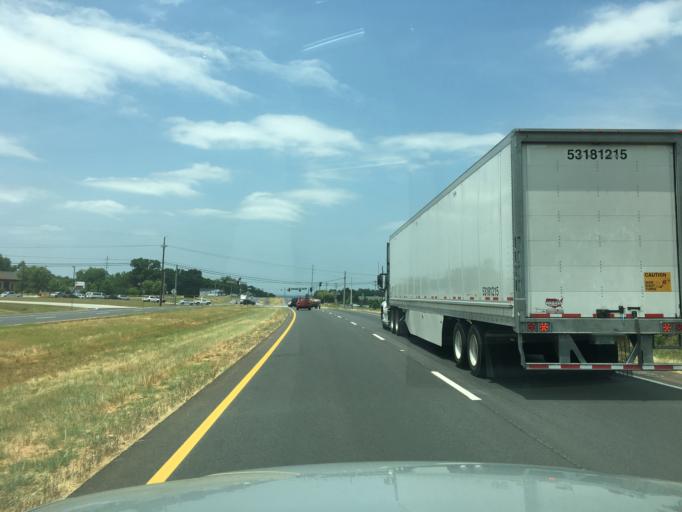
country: US
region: Georgia
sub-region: Jackson County
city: Commerce
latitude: 34.2323
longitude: -83.4514
